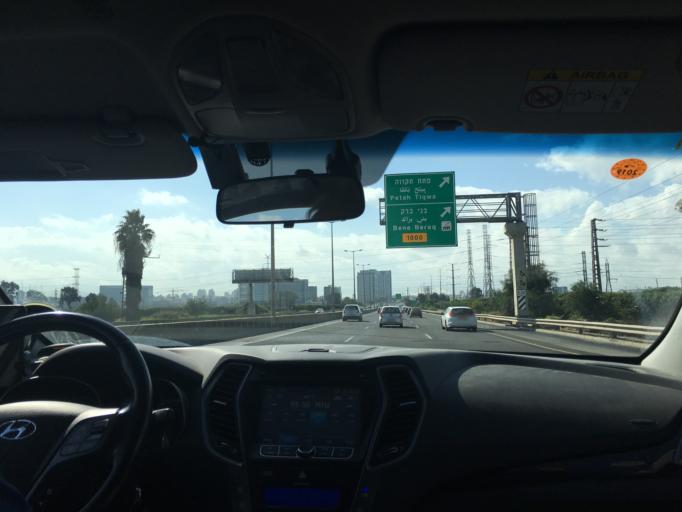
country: IL
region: Tel Aviv
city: Giv`at Shemu'el
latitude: 32.1119
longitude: 34.8503
